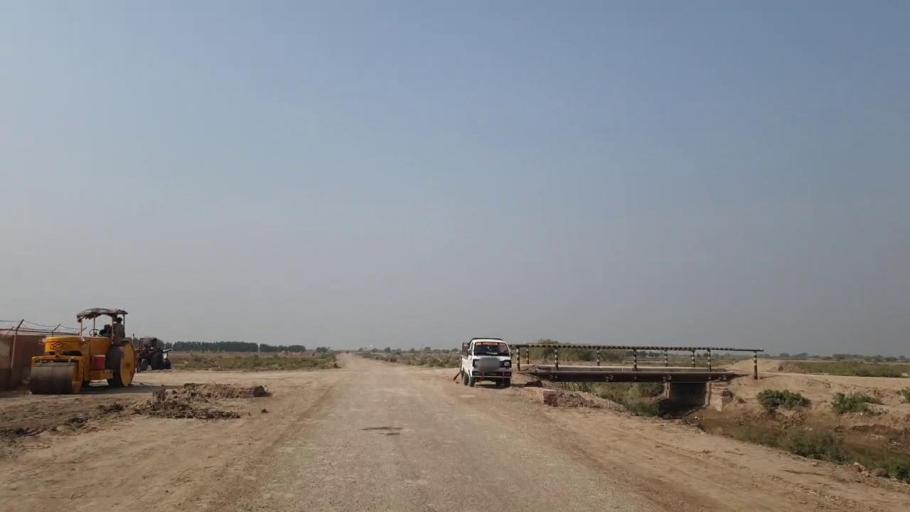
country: PK
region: Sindh
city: Tando Muhammad Khan
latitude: 24.9694
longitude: 68.5105
